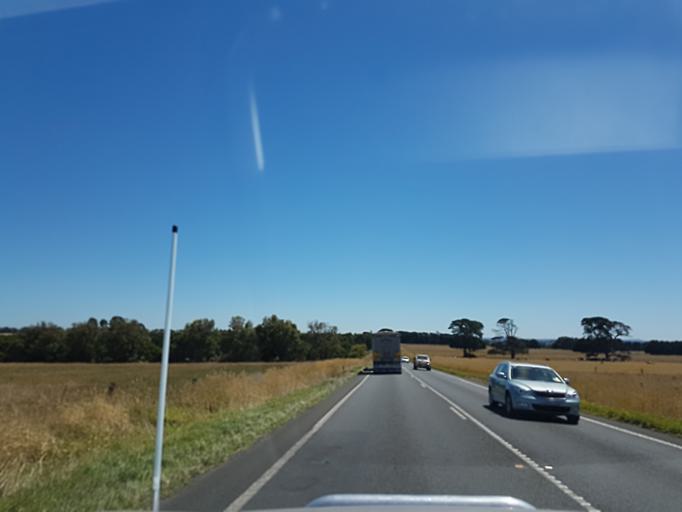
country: AU
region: Victoria
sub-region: Colac-Otway
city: Colac
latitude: -38.3365
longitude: 143.5117
